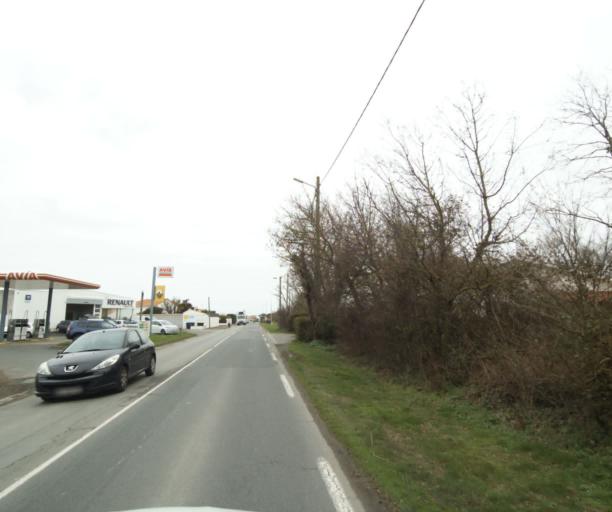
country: FR
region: Poitou-Charentes
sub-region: Departement de la Charente-Maritime
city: Nieul-sur-Mer
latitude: 46.1982
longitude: -1.1584
